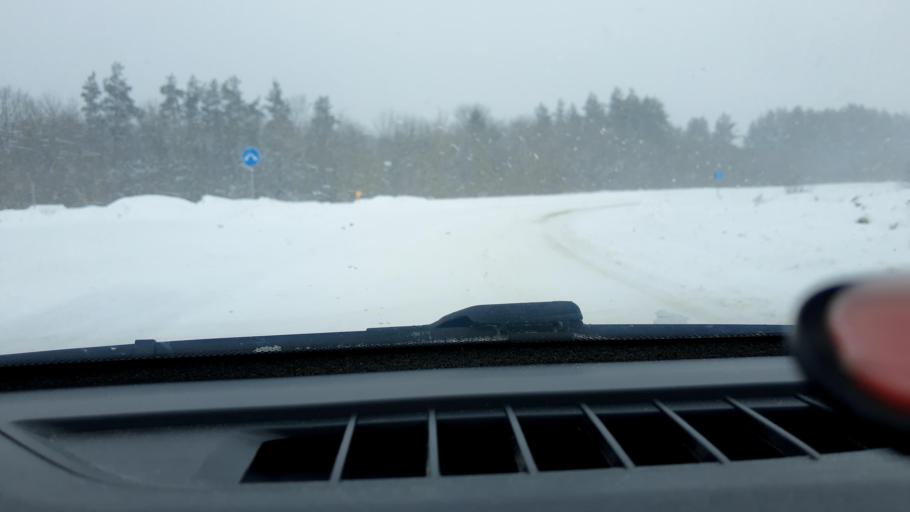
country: RU
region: Nizjnij Novgorod
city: Buturlino
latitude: 55.5961
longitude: 44.8826
